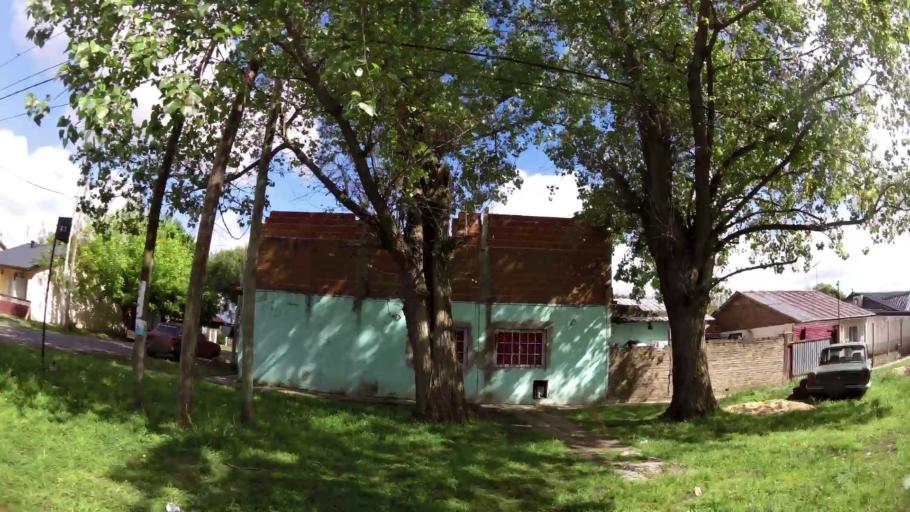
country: AR
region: Buenos Aires
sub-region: Partido de Quilmes
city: Quilmes
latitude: -34.7987
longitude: -58.1571
